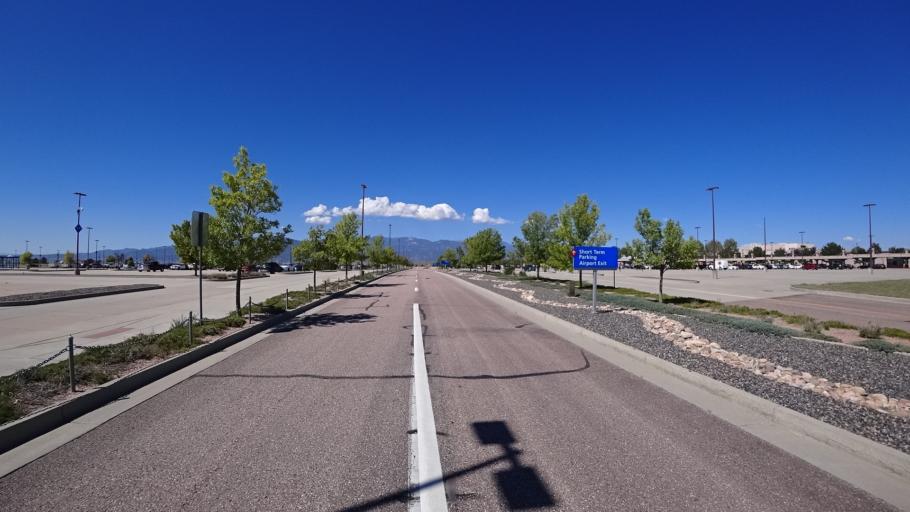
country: US
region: Colorado
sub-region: El Paso County
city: Security-Widefield
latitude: 38.7952
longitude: -104.6981
